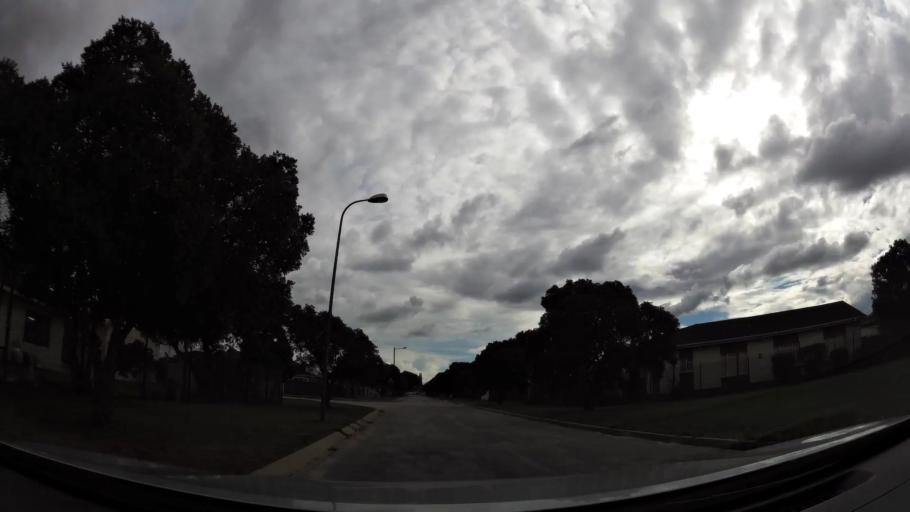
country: ZA
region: Eastern Cape
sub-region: Nelson Mandela Bay Metropolitan Municipality
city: Port Elizabeth
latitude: -33.9348
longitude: 25.5157
